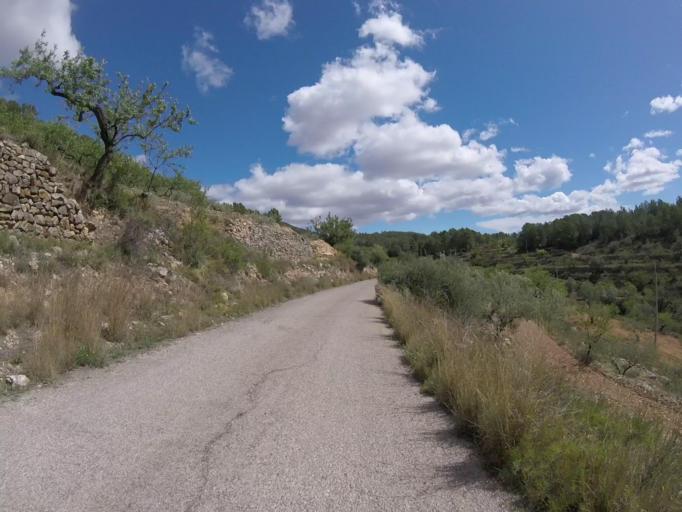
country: ES
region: Valencia
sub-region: Provincia de Castello
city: Sierra-Engarceran
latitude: 40.2700
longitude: -0.0994
